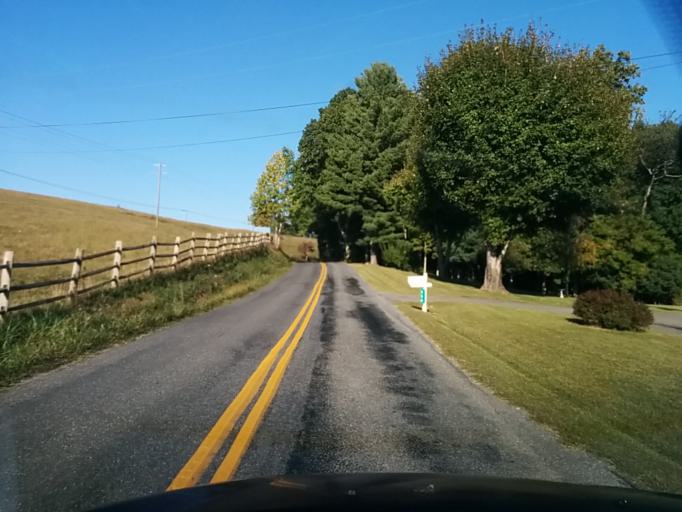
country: US
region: Virginia
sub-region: City of Lexington
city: Lexington
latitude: 37.7440
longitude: -79.5391
